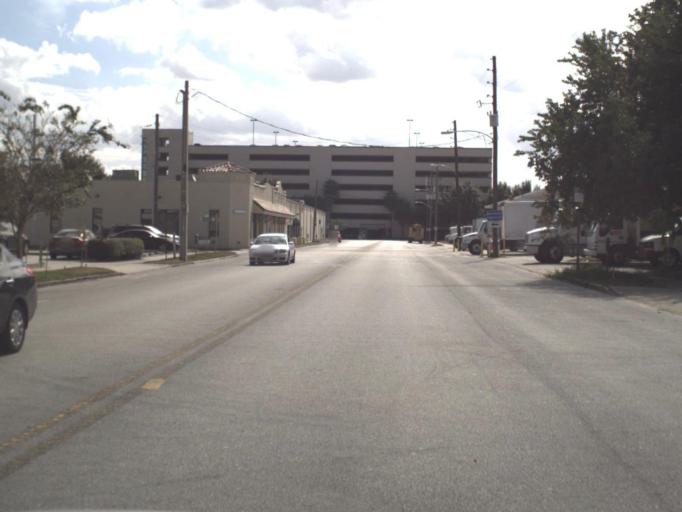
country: US
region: Florida
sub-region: Orange County
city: Orlando
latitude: 28.5256
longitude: -81.3814
